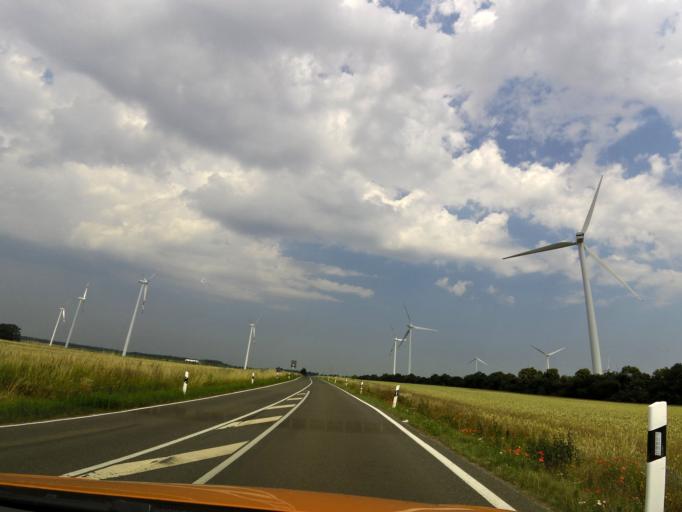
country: DE
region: Brandenburg
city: Nauen
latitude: 52.5419
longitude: 12.8761
